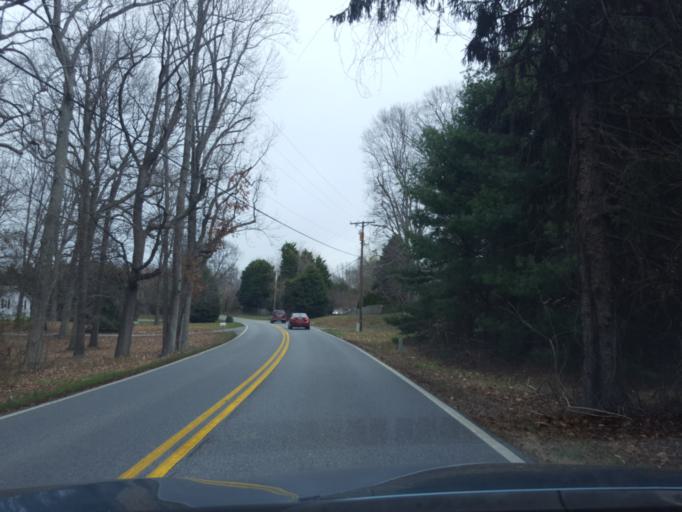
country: US
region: Maryland
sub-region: Calvert County
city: Owings
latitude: 38.7113
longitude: -76.5669
